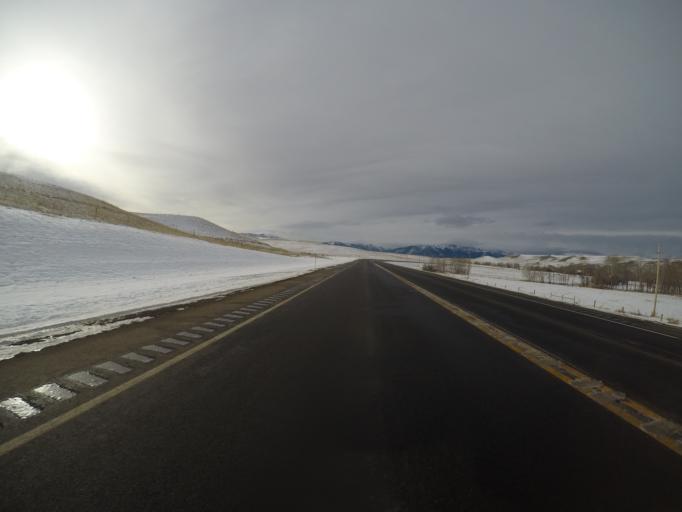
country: US
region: Montana
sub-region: Stillwater County
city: Absarokee
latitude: 45.4374
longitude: -109.4584
